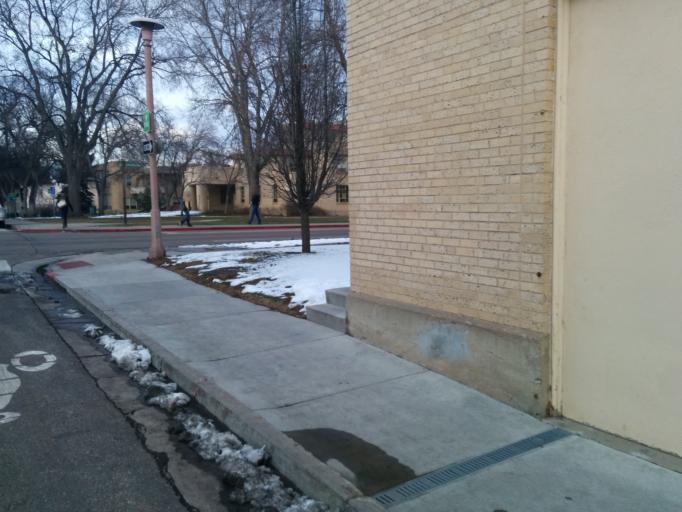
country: US
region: Colorado
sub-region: Larimer County
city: Fort Collins
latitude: 40.5735
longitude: -105.0803
